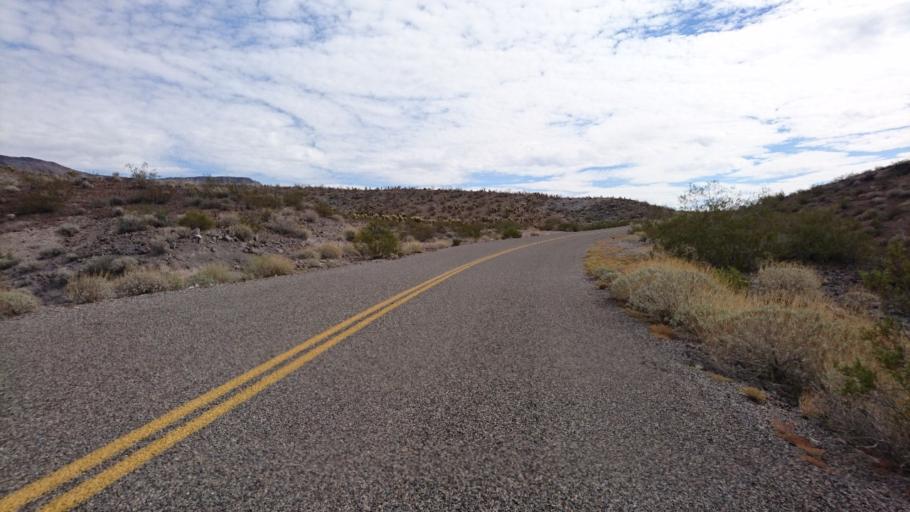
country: US
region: Arizona
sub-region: Mohave County
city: Mohave Valley
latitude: 34.9637
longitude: -114.4098
